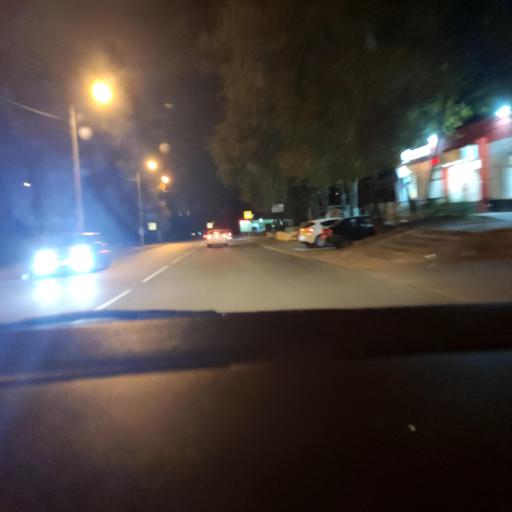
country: RU
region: Voronezj
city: Podgornoye
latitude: 51.6976
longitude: 39.1487
